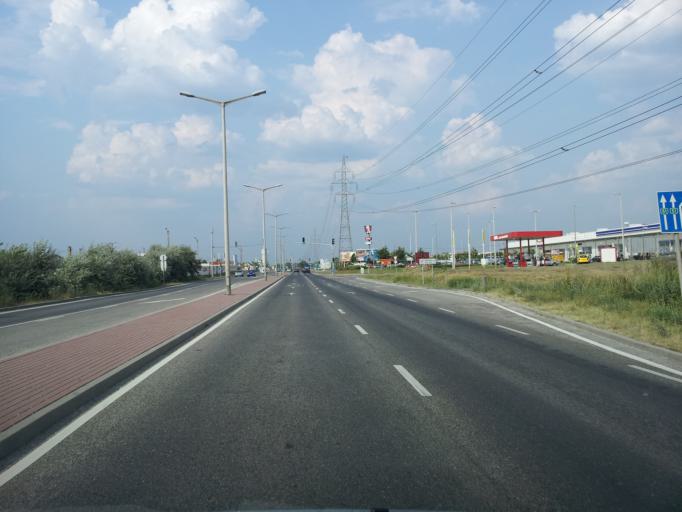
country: HU
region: Pest
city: Dunaharaszti
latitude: 47.3433
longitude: 19.1157
